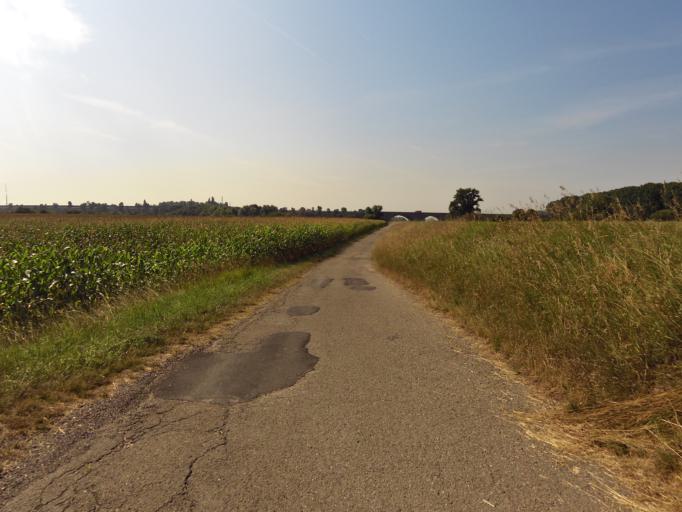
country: DE
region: Hesse
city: Lampertheim
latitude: 49.5563
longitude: 8.4209
